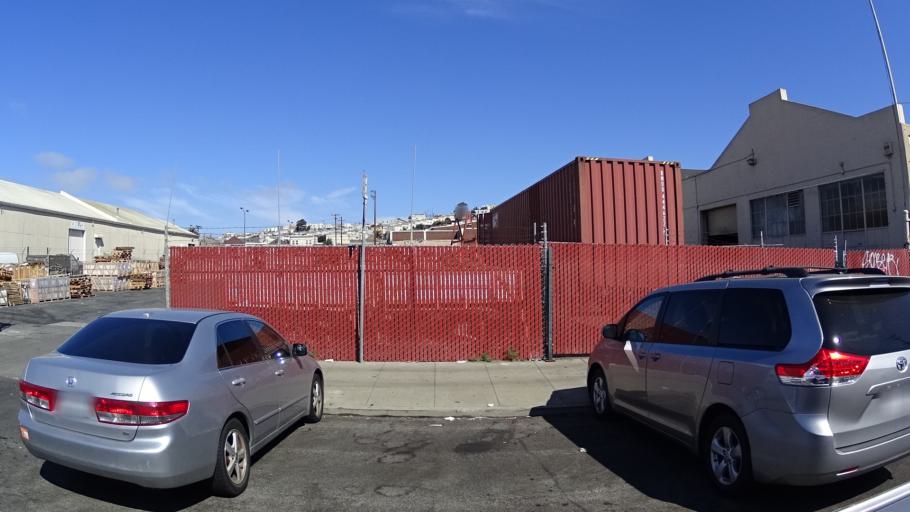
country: US
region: California
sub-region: San Mateo County
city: Brisbane
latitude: 37.7287
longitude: -122.3993
